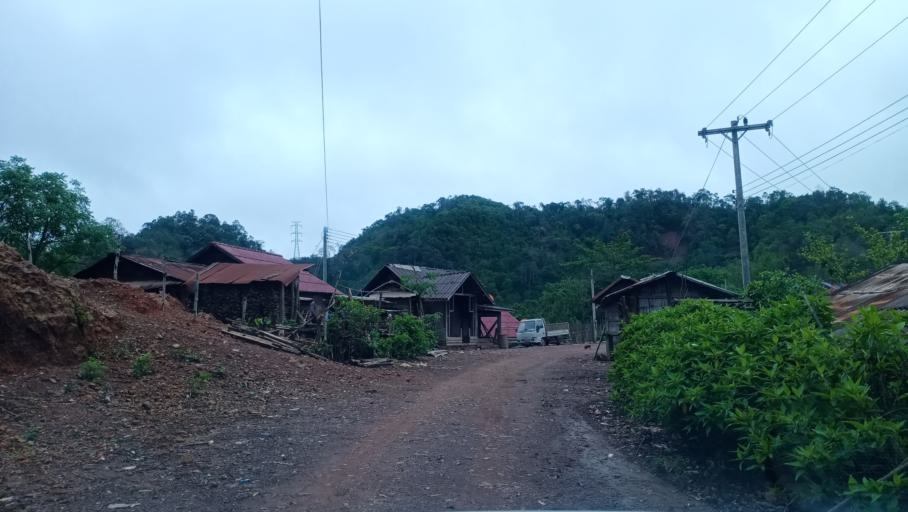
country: LA
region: Phongsali
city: Phongsali
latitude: 21.3459
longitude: 102.0917
